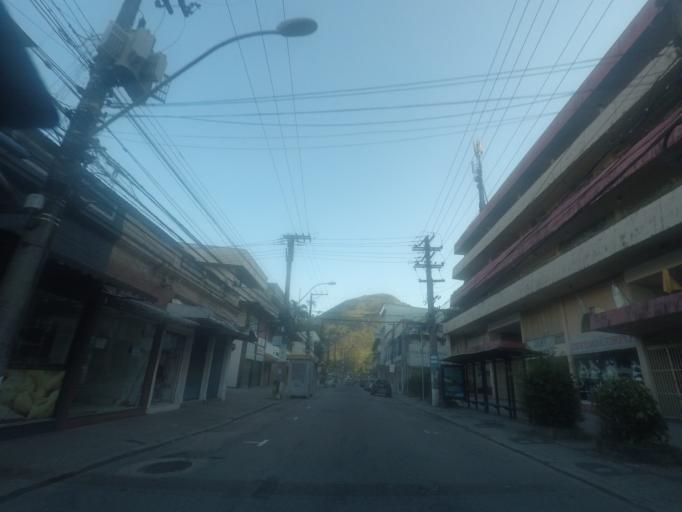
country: BR
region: Rio de Janeiro
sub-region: Petropolis
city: Petropolis
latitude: -22.5166
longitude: -43.1704
